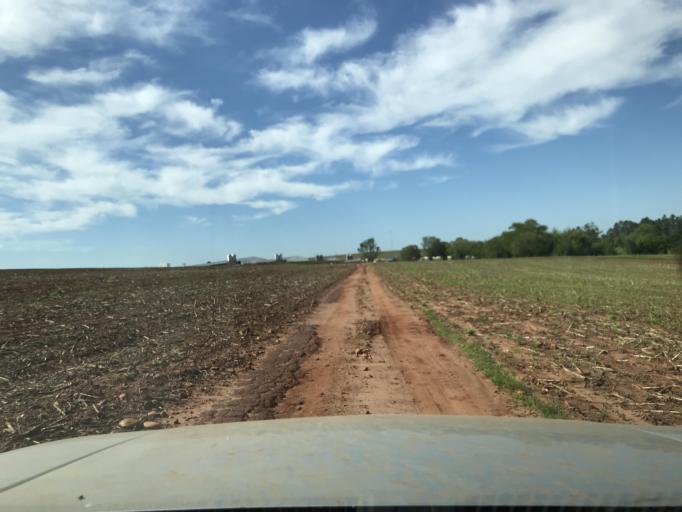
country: BR
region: Parana
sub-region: Palotina
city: Palotina
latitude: -24.1762
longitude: -53.8388
